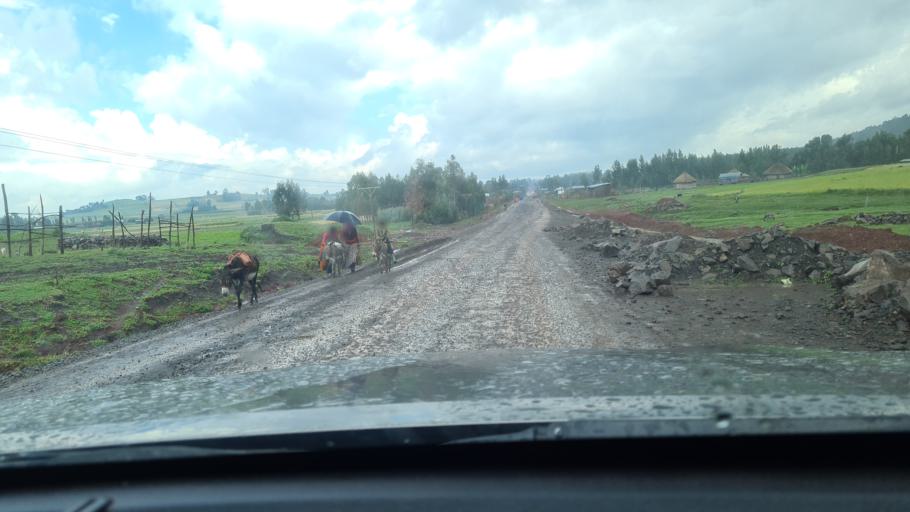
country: ET
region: Oromiya
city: Huruta
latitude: 8.0785
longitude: 39.5458
